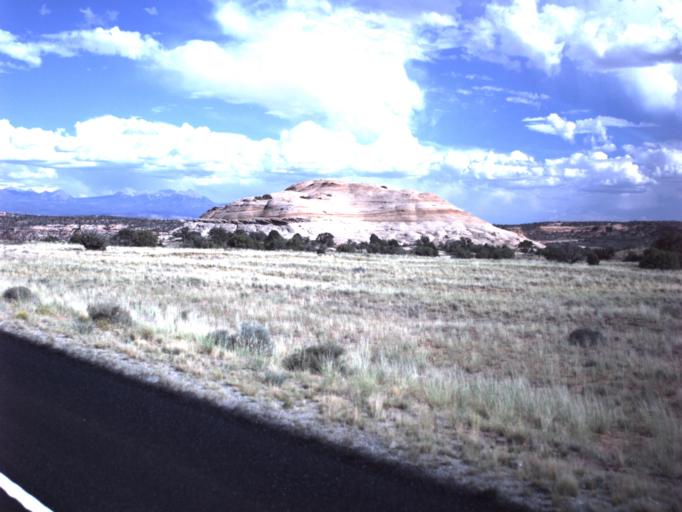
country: US
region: Utah
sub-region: Grand County
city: Moab
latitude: 38.6370
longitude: -109.7561
